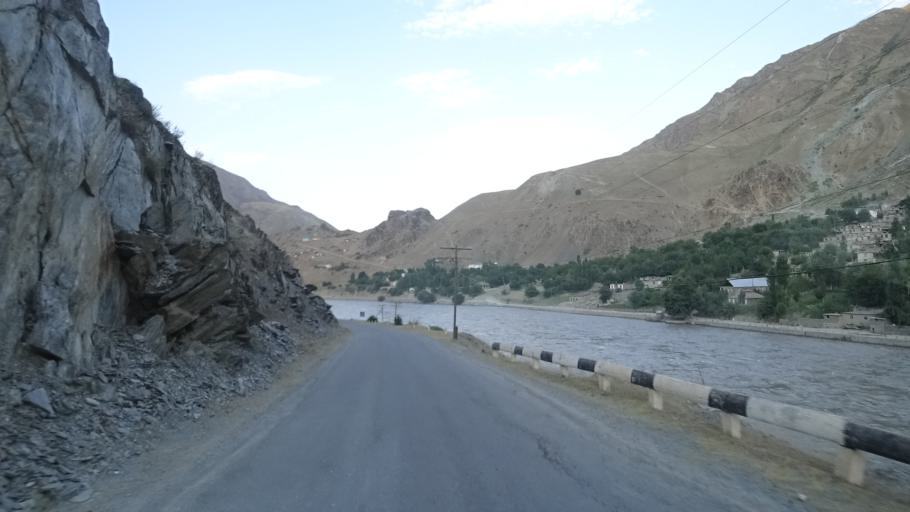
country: AF
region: Badakhshan
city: Nusay
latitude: 38.4451
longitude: 70.8130
